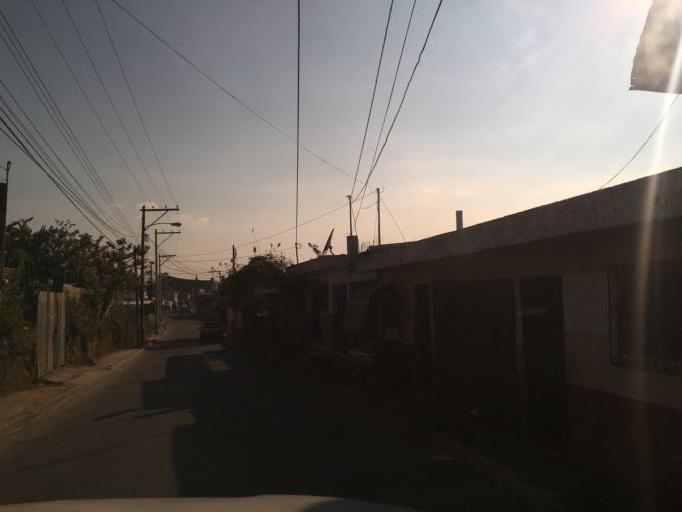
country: GT
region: Guatemala
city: Mixco
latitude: 14.6124
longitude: -90.5756
